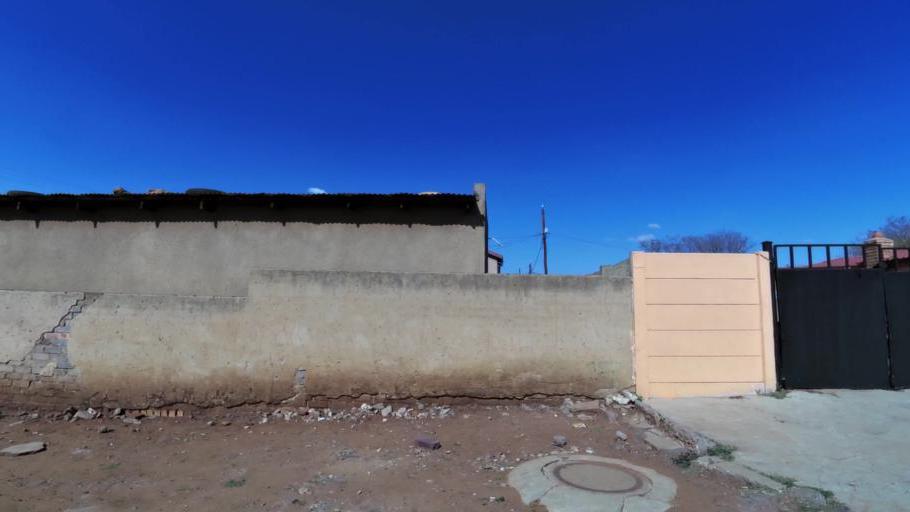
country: ZA
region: Gauteng
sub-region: City of Johannesburg Metropolitan Municipality
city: Soweto
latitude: -26.2367
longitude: 27.8864
